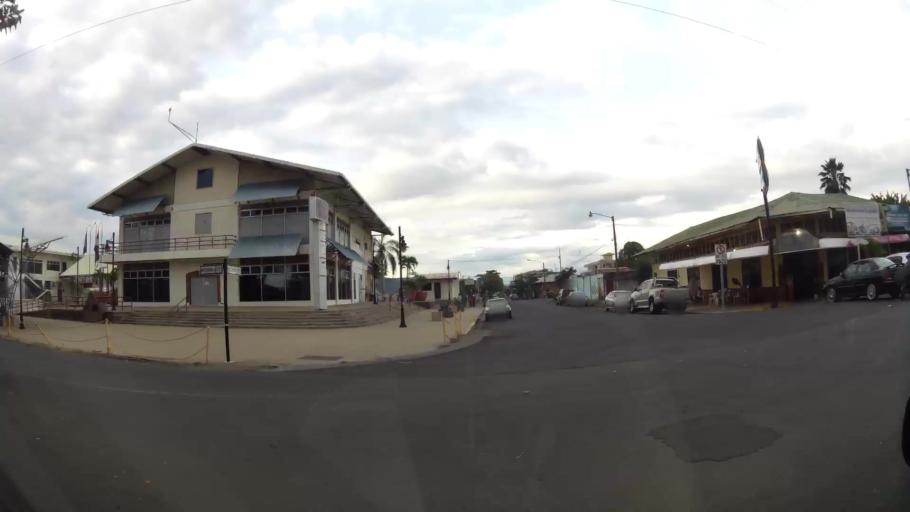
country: CR
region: Puntarenas
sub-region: Canton Central de Puntarenas
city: Puntarenas
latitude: 9.9755
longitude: -84.8316
